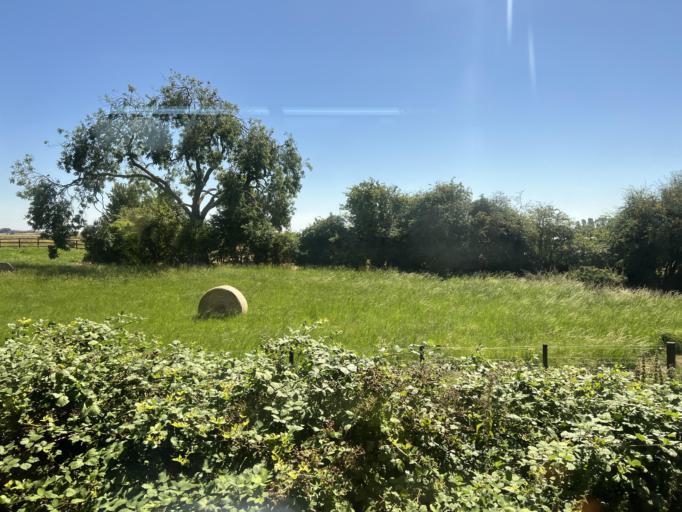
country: GB
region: England
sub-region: Lincolnshire
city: Wainfleet All Saints
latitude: 53.1047
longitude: 0.2392
